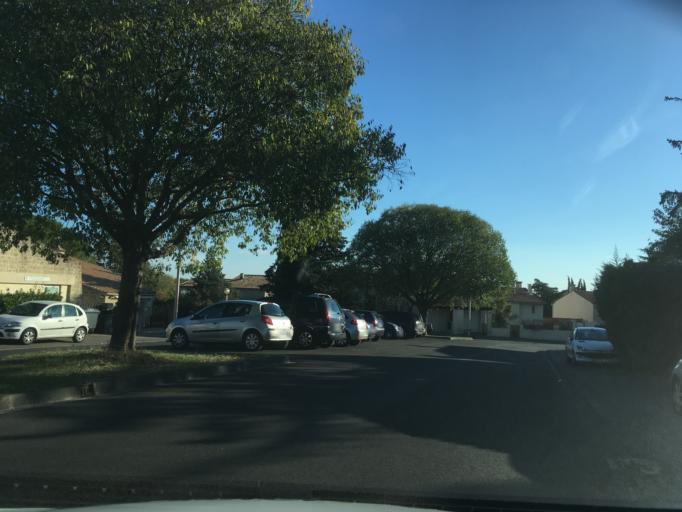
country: FR
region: Languedoc-Roussillon
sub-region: Departement de l'Herault
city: Grabels
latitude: 43.6404
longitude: 3.8212
